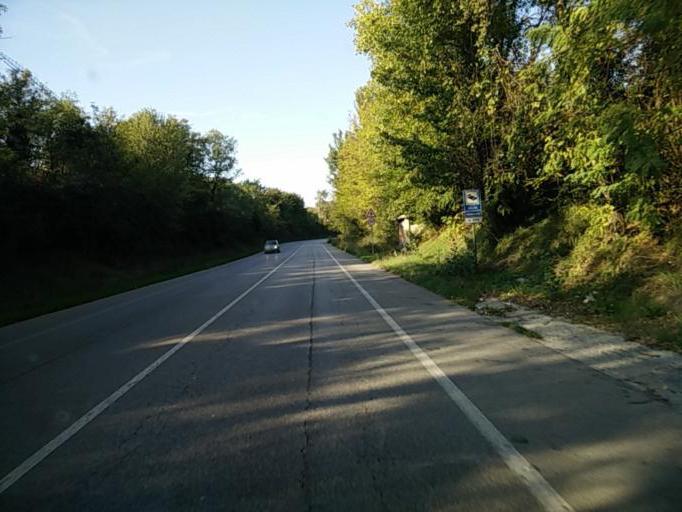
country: IT
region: Lombardy
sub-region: Provincia di Brescia
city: Desenzano del Garda
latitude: 45.4723
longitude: 10.5274
